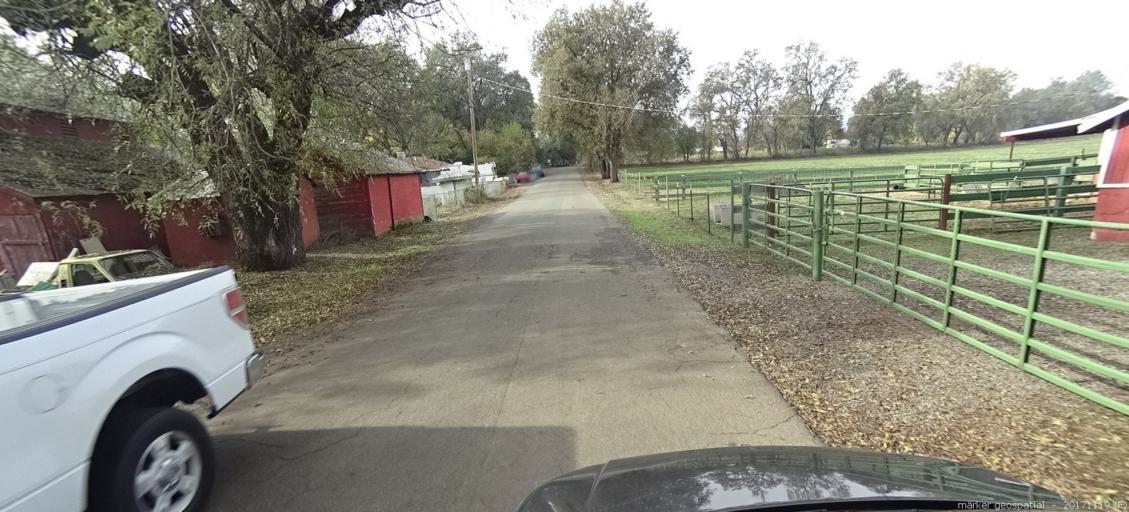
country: US
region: California
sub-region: Shasta County
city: Anderson
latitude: 40.4867
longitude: -122.3204
